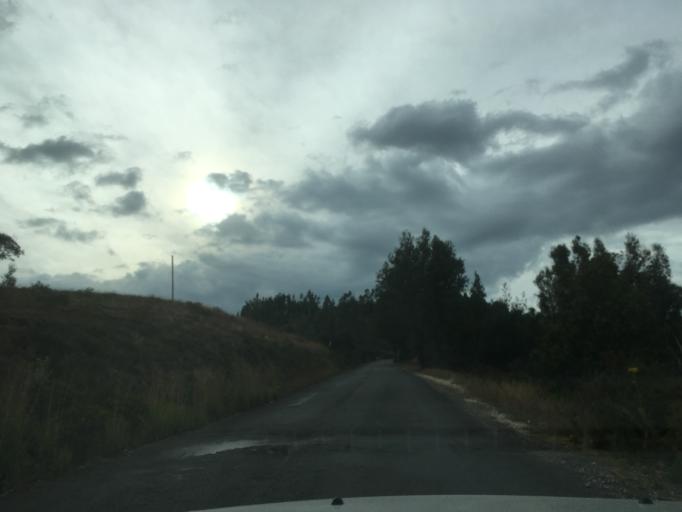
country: CO
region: Boyaca
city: Firavitoba
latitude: 5.6752
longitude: -73.0147
